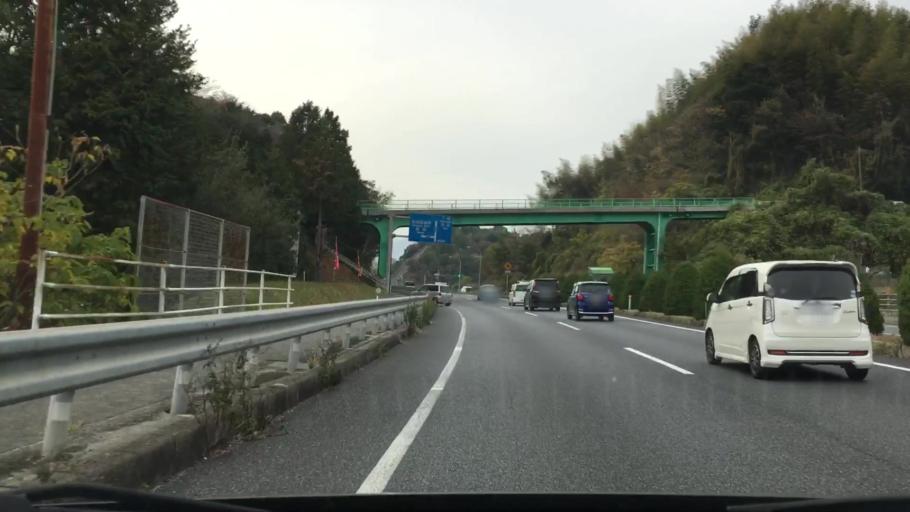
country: JP
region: Yamaguchi
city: Tokuyama
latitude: 34.0769
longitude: 131.7356
